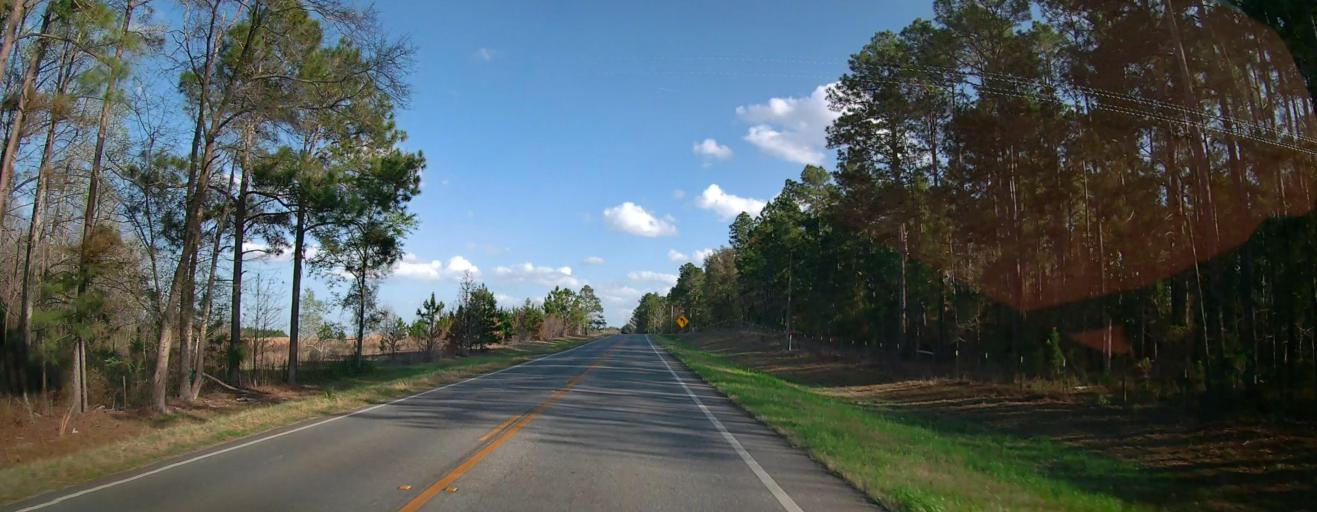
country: US
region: Georgia
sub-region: Toombs County
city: Lyons
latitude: 32.1778
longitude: -82.2876
